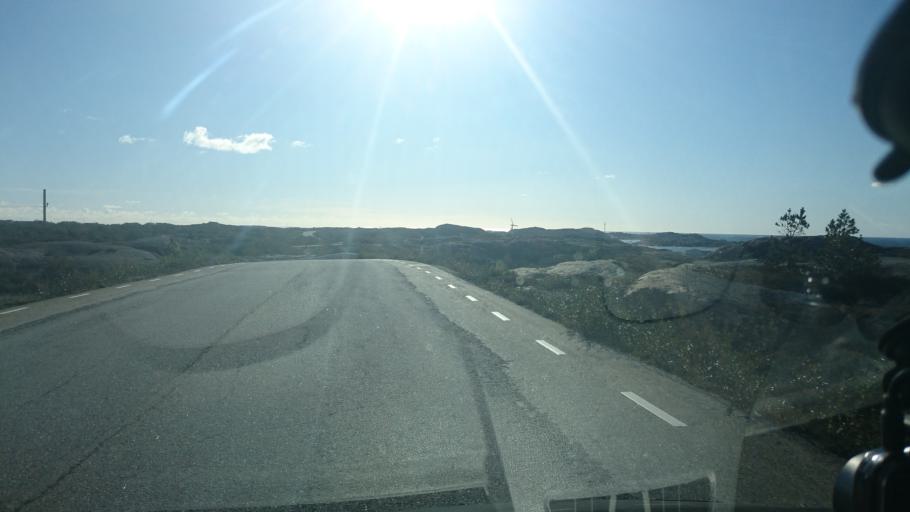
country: SE
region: Vaestra Goetaland
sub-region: Lysekils Kommun
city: Lysekil
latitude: 58.3221
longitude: 11.4150
